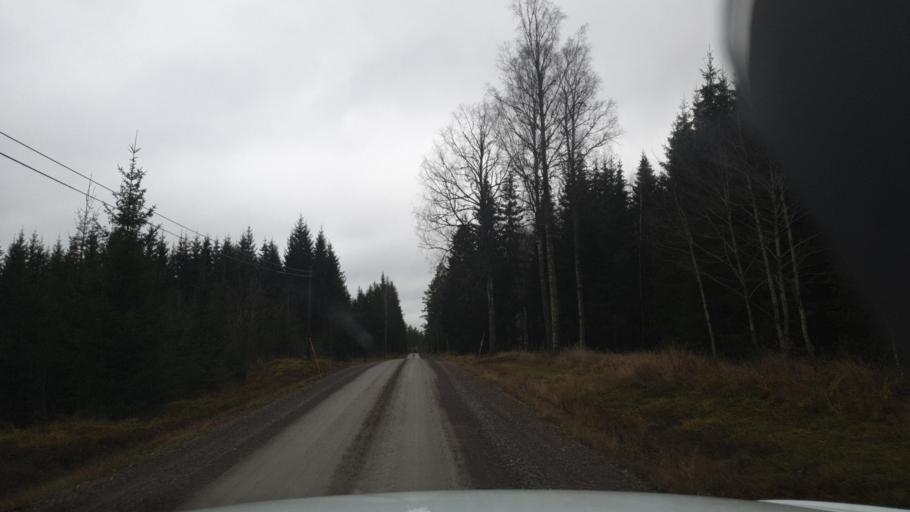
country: SE
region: Vaermland
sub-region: Eda Kommun
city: Charlottenberg
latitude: 59.9751
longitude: 12.4939
